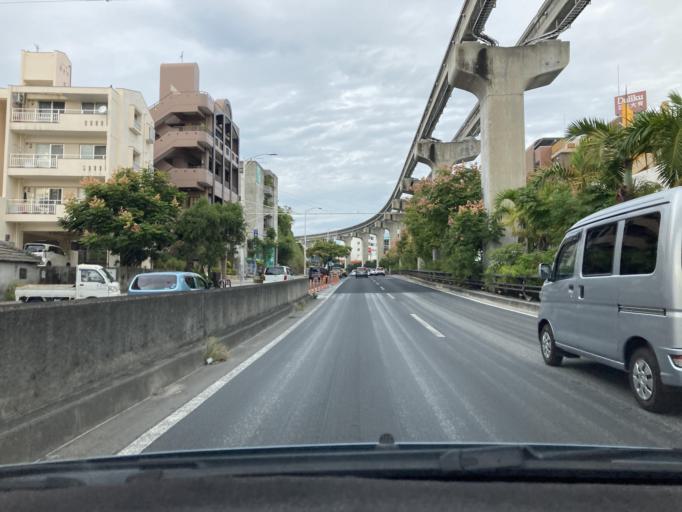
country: JP
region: Okinawa
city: Naha-shi
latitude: 26.2198
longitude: 127.6975
